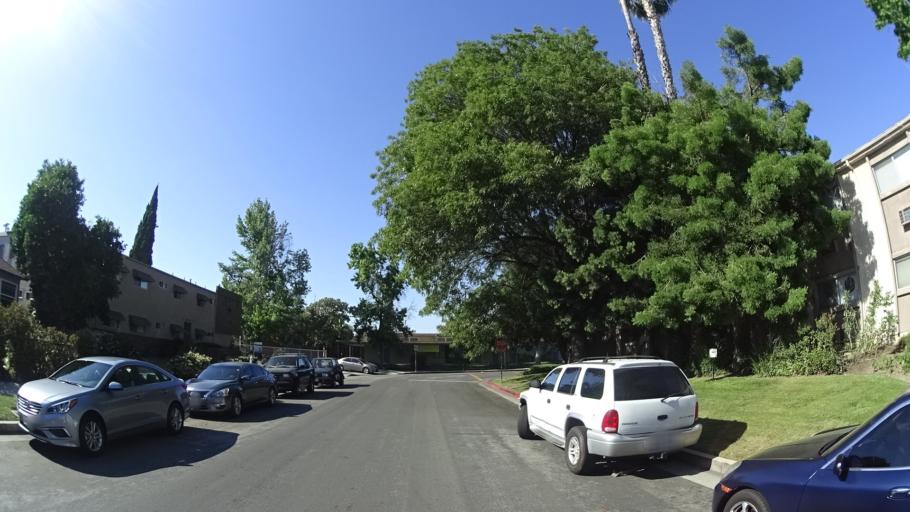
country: US
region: California
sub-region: Los Angeles County
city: North Hollywood
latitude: 34.1699
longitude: -118.3993
